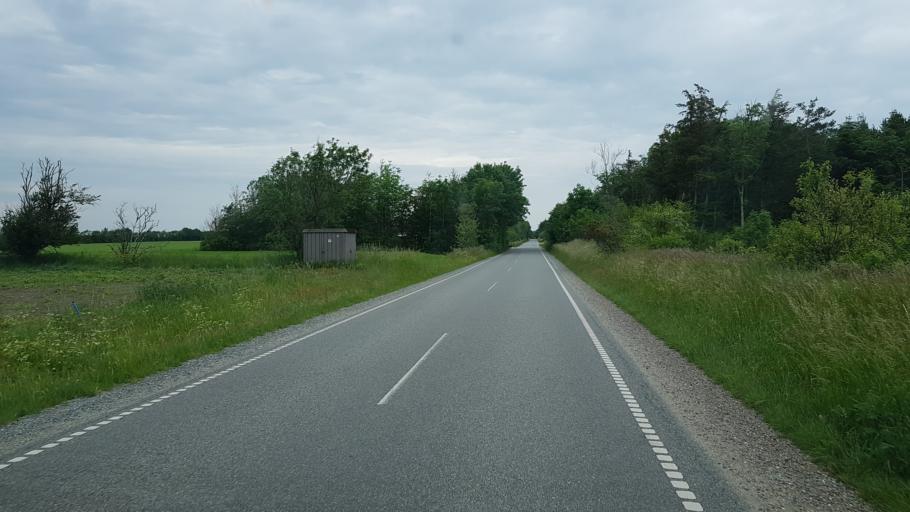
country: DK
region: South Denmark
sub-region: Varde Kommune
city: Oksbol
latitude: 55.6691
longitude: 8.3083
